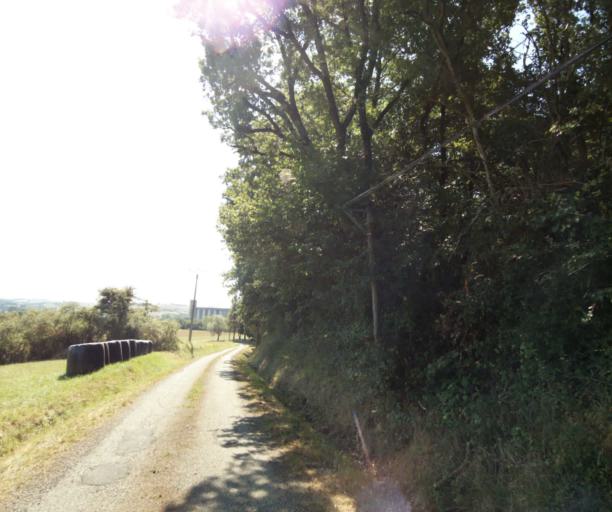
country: FR
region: Midi-Pyrenees
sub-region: Departement de l'Ariege
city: Lezat-sur-Leze
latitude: 43.2932
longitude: 1.3337
